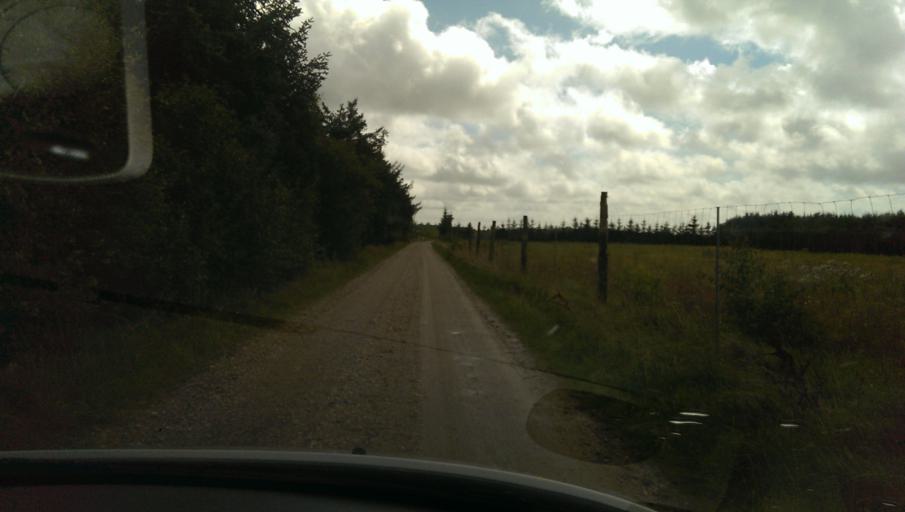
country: DK
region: South Denmark
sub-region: Varde Kommune
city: Varde
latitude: 55.6050
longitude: 8.4512
